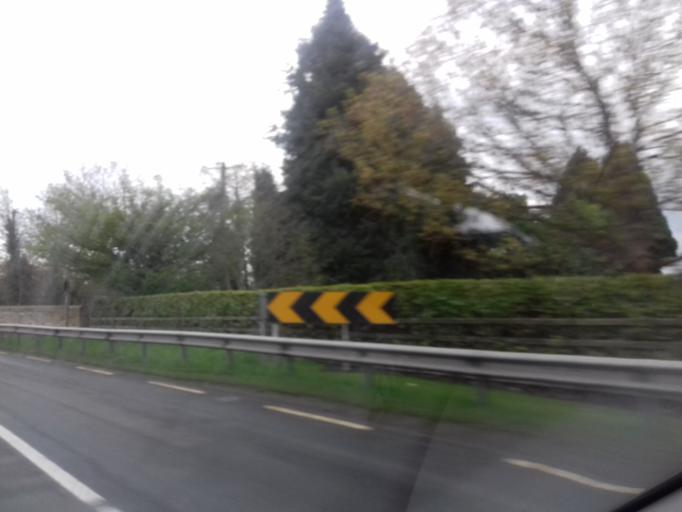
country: IE
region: Ulster
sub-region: An Cabhan
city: Ballyconnell
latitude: 54.0931
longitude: -7.5523
